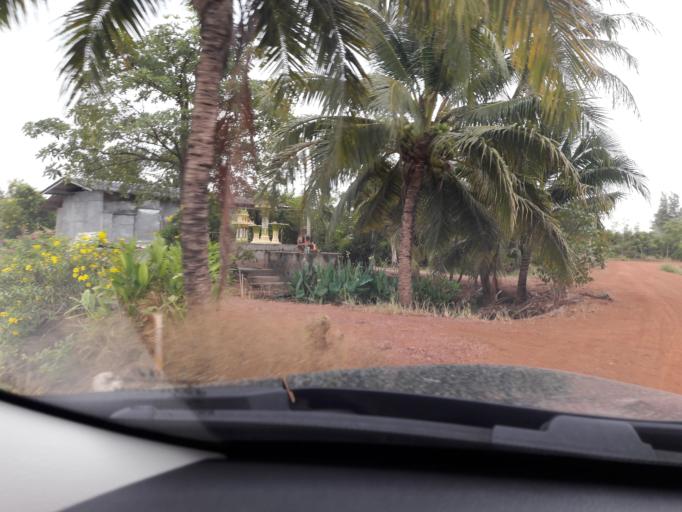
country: TH
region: Ratchaburi
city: Bang Phae
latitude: 13.6159
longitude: 99.9655
